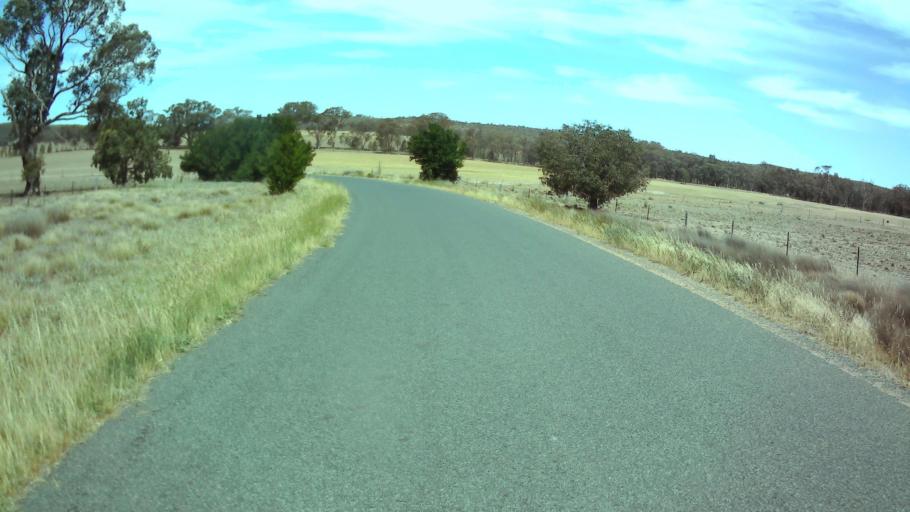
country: AU
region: New South Wales
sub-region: Weddin
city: Grenfell
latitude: -33.8438
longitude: 148.1776
